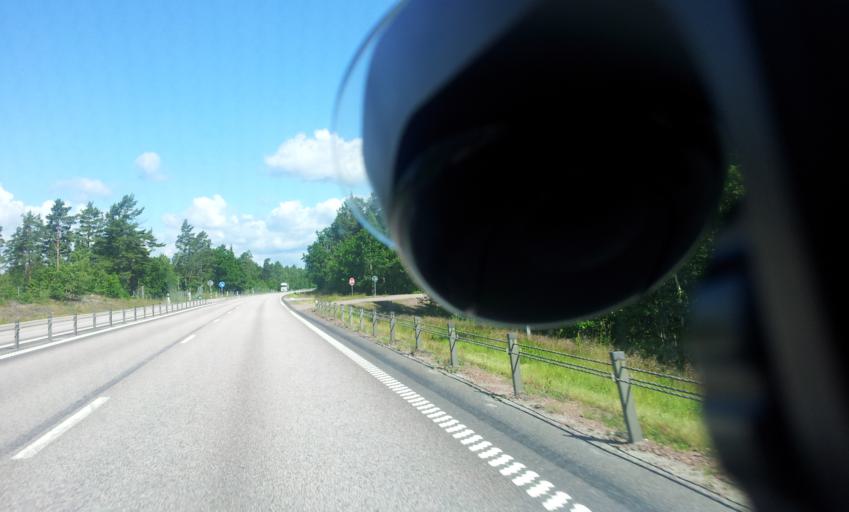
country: SE
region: Kalmar
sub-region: Oskarshamns Kommun
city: Paskallavik
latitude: 57.2092
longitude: 16.4361
